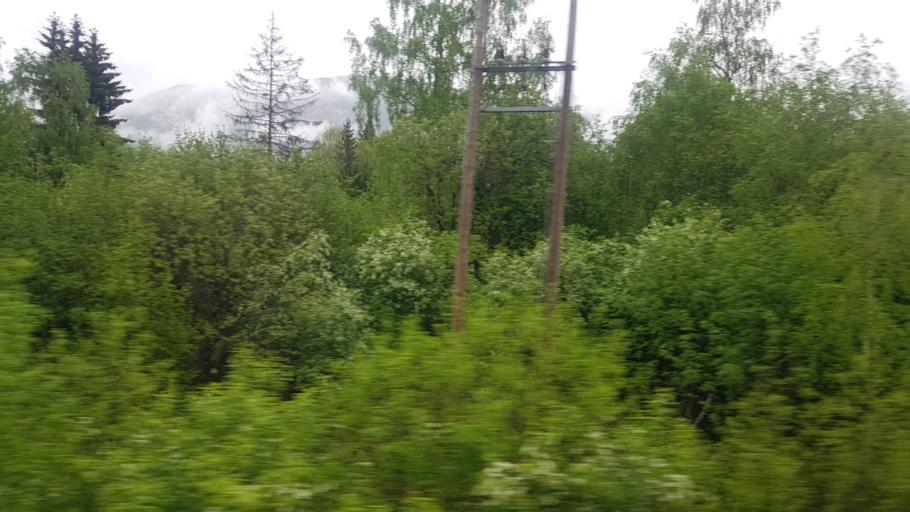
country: NO
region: Oppland
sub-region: Ringebu
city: Ringebu
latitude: 61.4440
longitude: 10.2040
